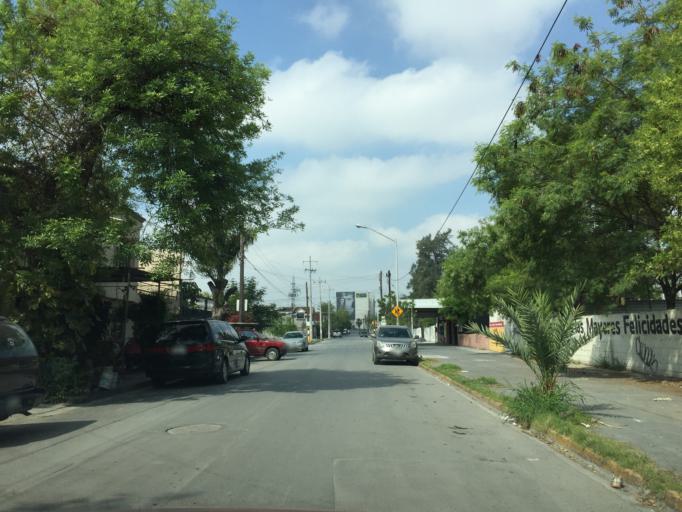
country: MX
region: Nuevo Leon
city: Guadalupe
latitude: 25.7062
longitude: -100.2205
